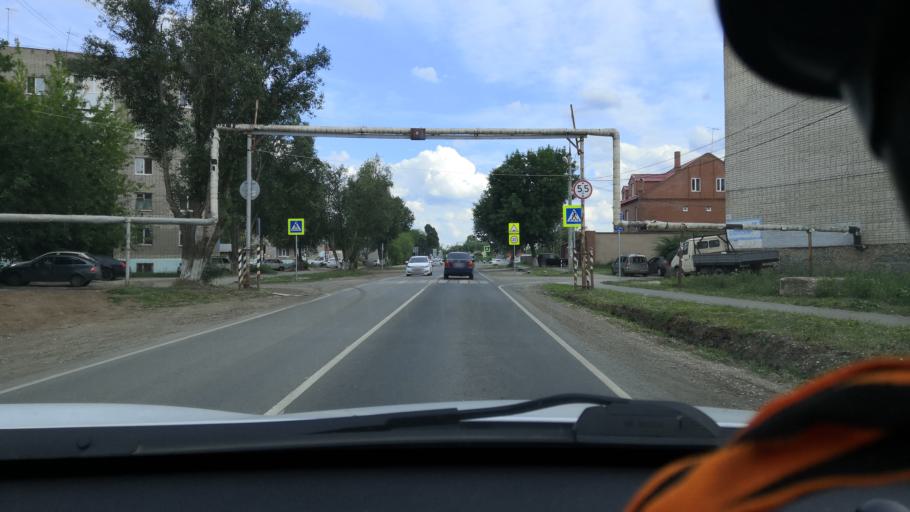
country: RU
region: Samara
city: Novosemeykino
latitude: 53.3717
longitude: 50.3514
